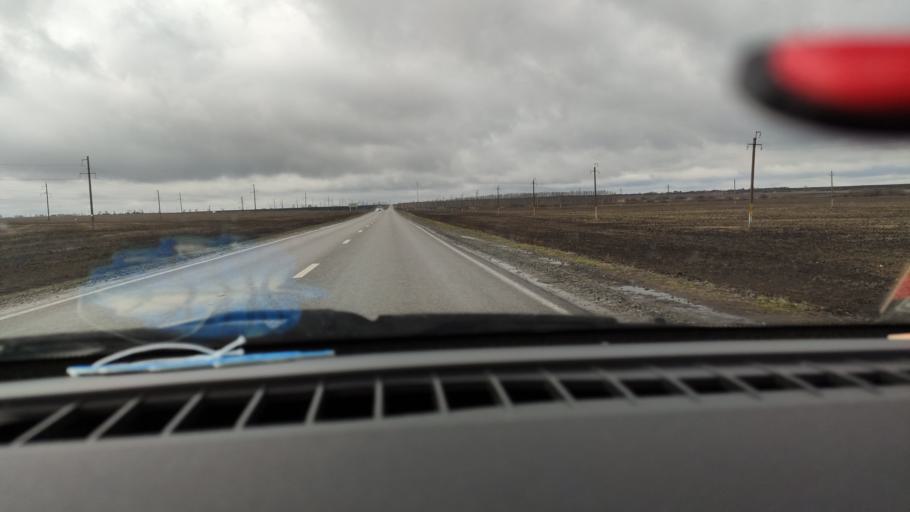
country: RU
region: Tatarstan
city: Nurlat
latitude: 54.4635
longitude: 50.8335
